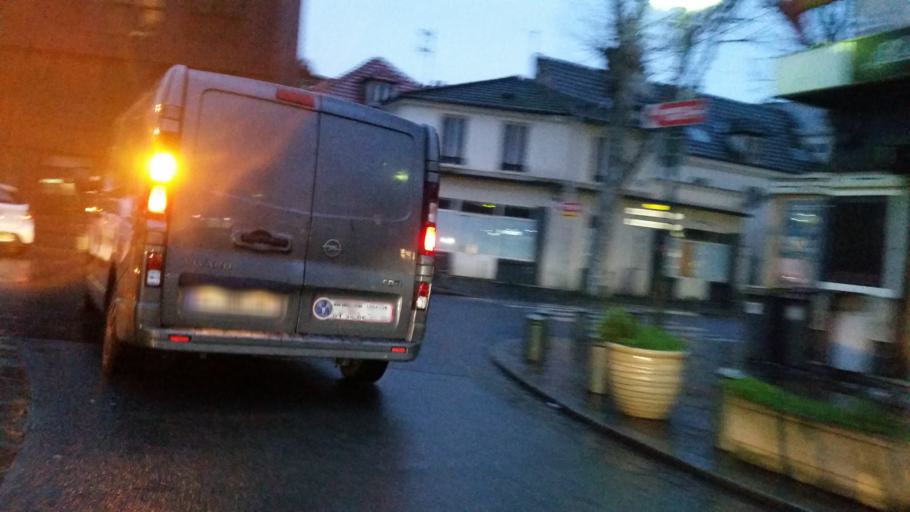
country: FR
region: Ile-de-France
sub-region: Departement du Val-de-Marne
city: Ivry-sur-Seine
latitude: 48.8072
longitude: 2.3916
